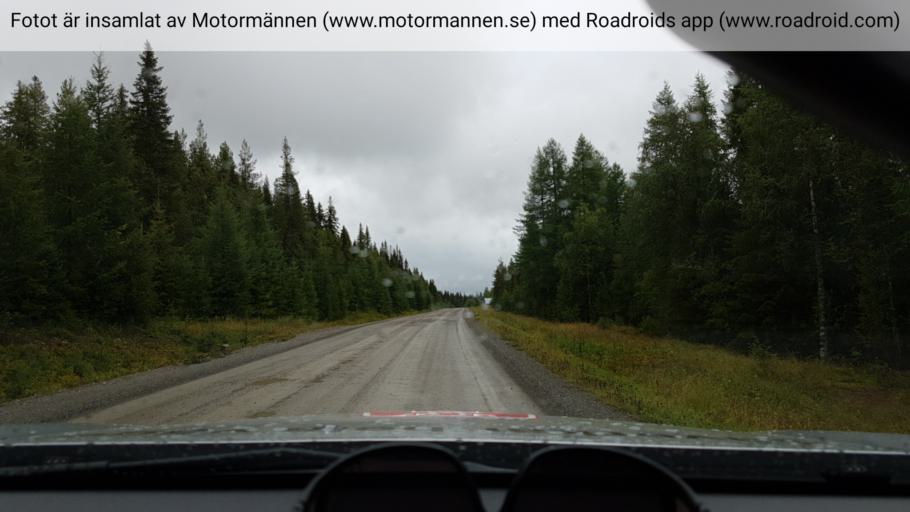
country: SE
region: Vaesterbotten
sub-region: Storumans Kommun
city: Storuman
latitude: 64.8574
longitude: 17.3855
